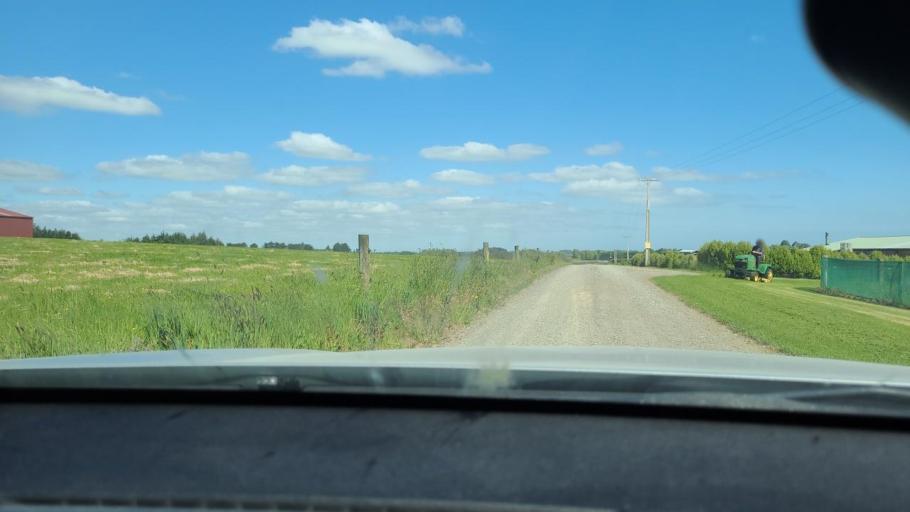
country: NZ
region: Southland
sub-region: Southland District
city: Riverton
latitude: -46.2777
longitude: 168.1354
